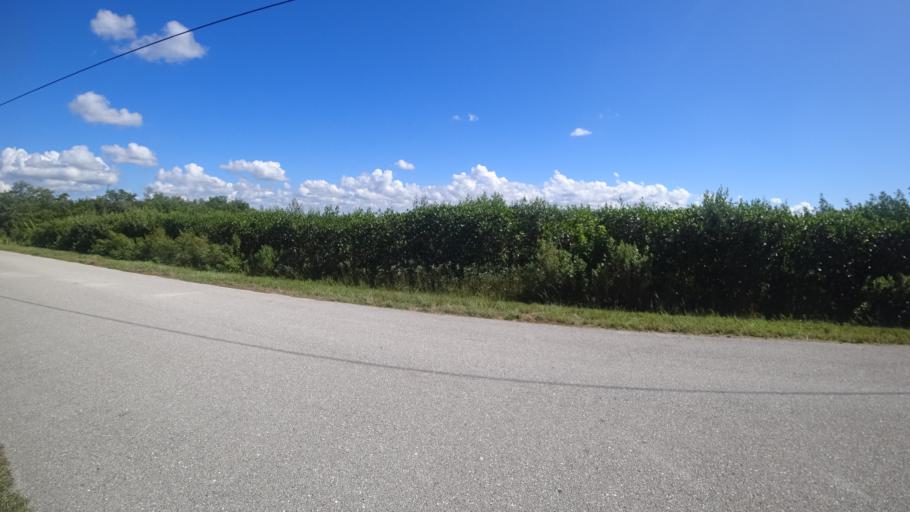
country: US
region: Florida
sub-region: Manatee County
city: Memphis
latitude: 27.5762
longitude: -82.5672
